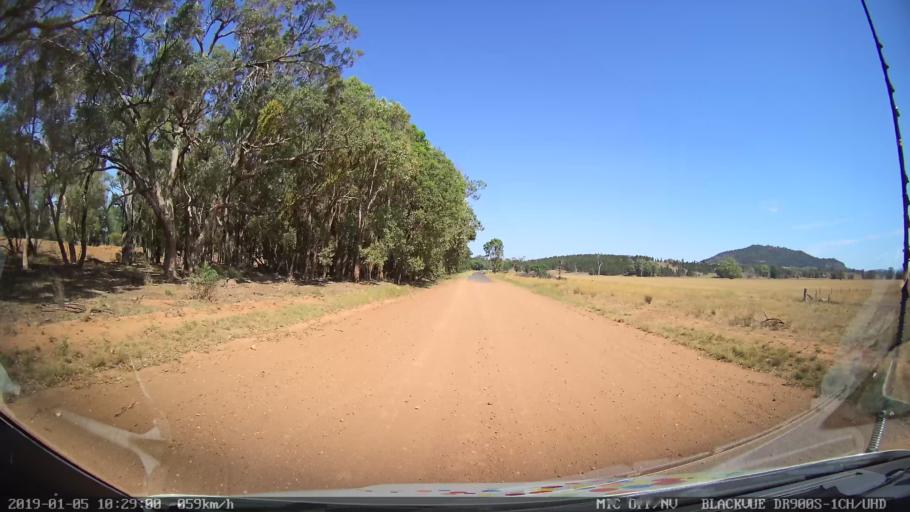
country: AU
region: New South Wales
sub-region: Gilgandra
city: Gilgandra
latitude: -31.5421
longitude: 148.9340
